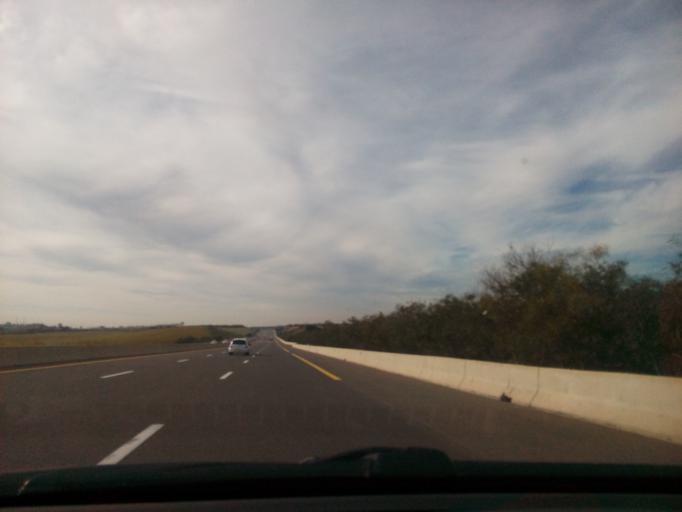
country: DZ
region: Sidi Bel Abbes
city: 'Ain el Berd
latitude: 35.3144
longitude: -0.5473
